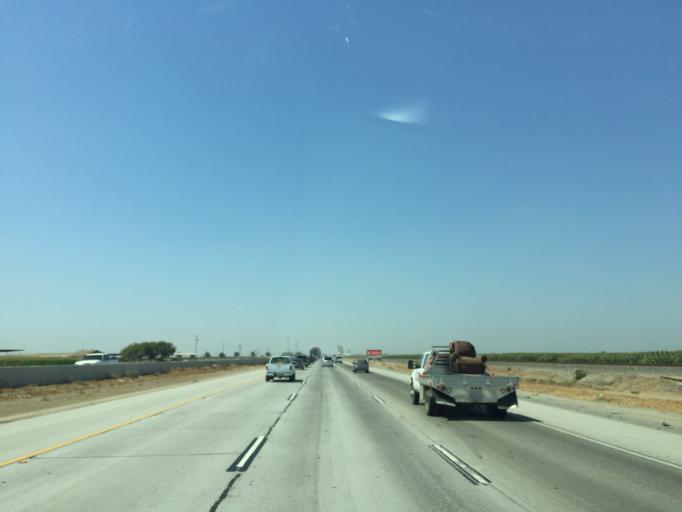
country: US
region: California
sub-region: Tulare County
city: London
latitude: 36.4180
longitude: -119.4652
